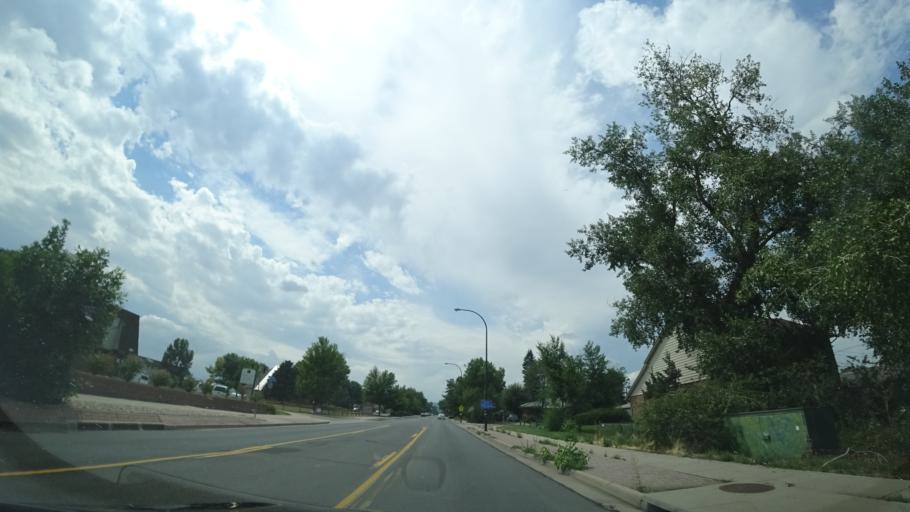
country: US
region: Colorado
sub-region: Jefferson County
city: Lakewood
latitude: 39.6967
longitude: -105.0743
